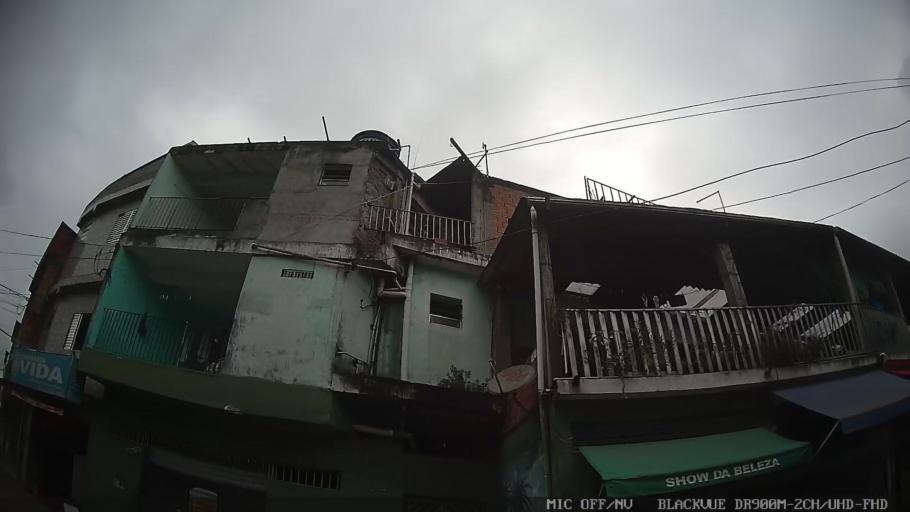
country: BR
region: Sao Paulo
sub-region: Osasco
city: Osasco
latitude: -23.4920
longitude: -46.7907
